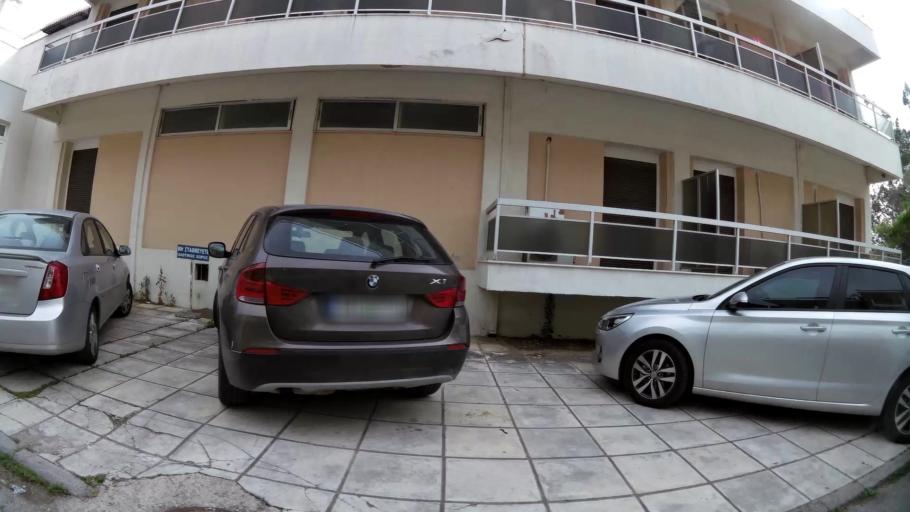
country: GR
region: Central Macedonia
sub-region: Nomos Thessalonikis
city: Oraiokastro
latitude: 40.7323
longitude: 22.9234
